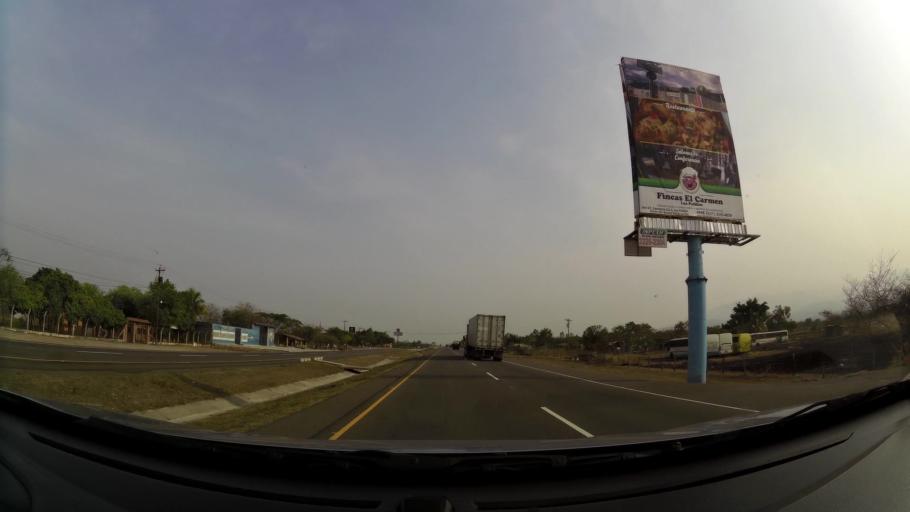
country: HN
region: Comayagua
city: Villa de San Antonio
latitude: 14.3306
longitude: -87.5881
